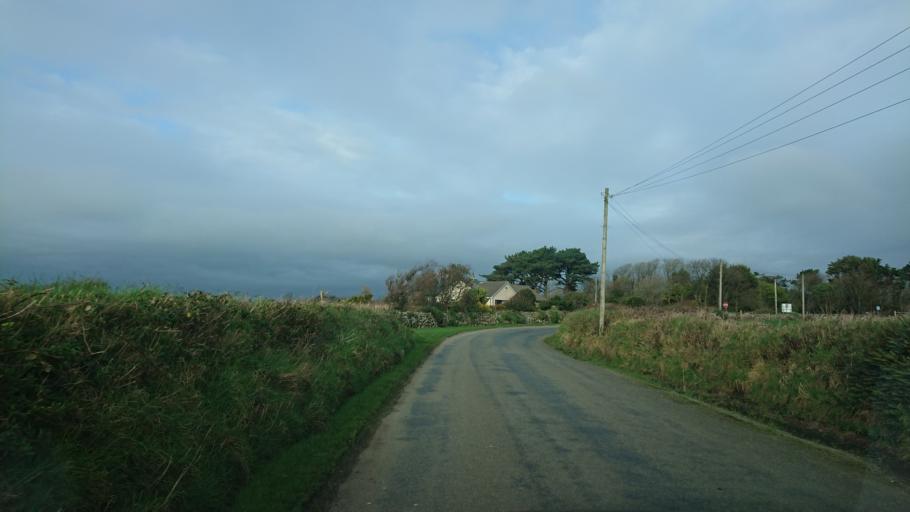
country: IE
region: Munster
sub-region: Waterford
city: Tra Mhor
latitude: 52.1546
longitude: -7.2154
